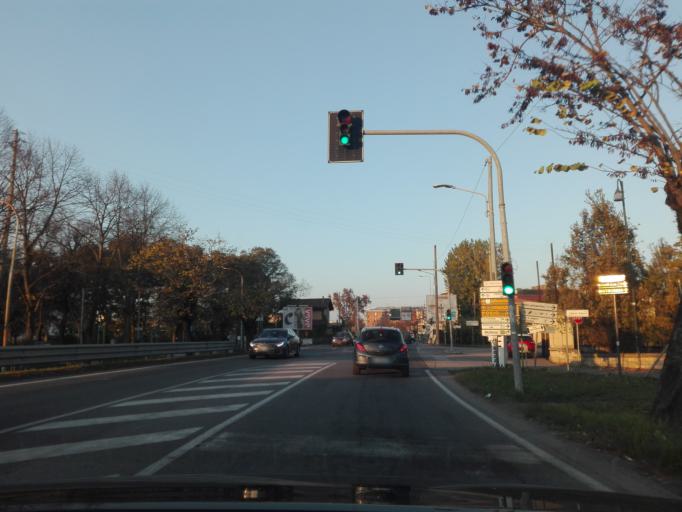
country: IT
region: Lombardy
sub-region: Provincia di Mantova
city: Mantova
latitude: 45.1436
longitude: 10.7947
